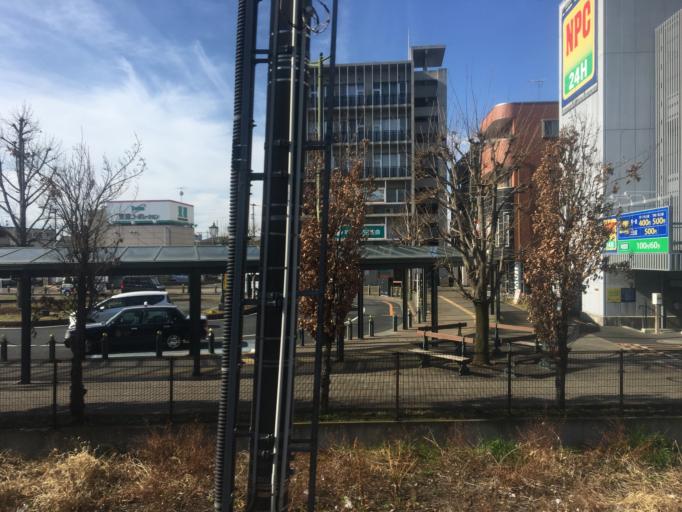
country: JP
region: Saitama
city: Sakado
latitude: 35.9493
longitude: 139.4081
